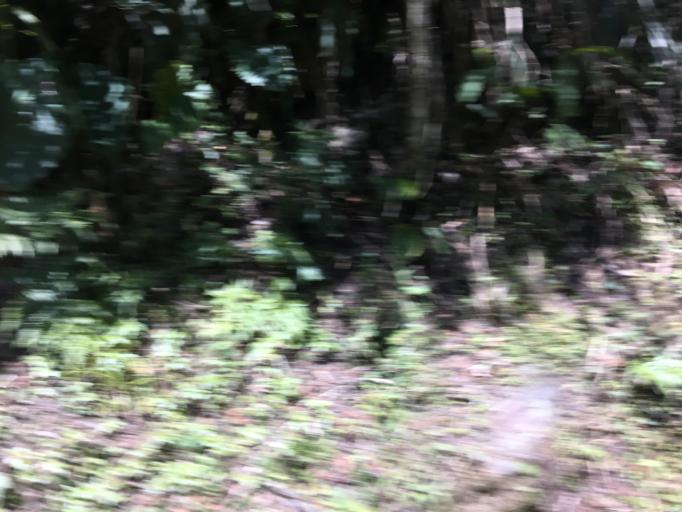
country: TW
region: Taiwan
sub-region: Yilan
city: Yilan
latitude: 24.5389
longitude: 121.5165
